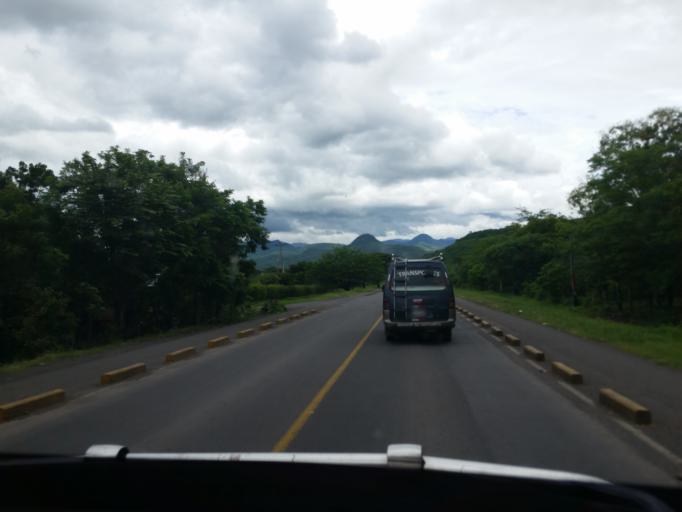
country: NI
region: Matagalpa
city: Ciudad Dario
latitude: 12.8711
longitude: -86.0886
